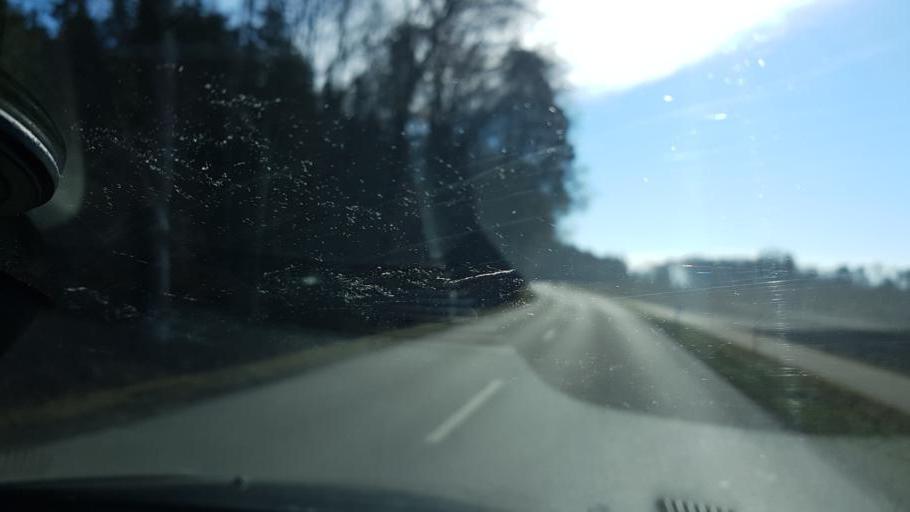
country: DE
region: Bavaria
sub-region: Upper Bavaria
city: Oberschweinbach
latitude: 48.2263
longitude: 11.1719
